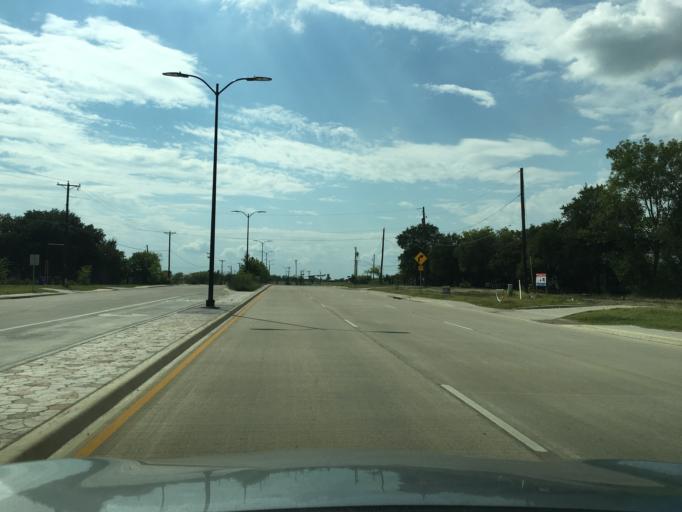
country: US
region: Texas
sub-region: Denton County
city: Oak Point
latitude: 33.1665
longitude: -96.9728
